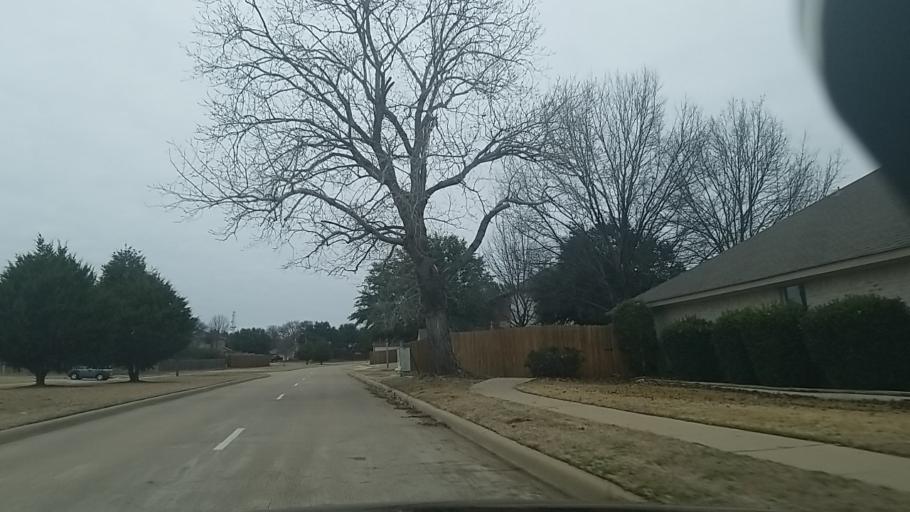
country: US
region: Texas
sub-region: Denton County
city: Corinth
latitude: 33.1389
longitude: -97.0775
